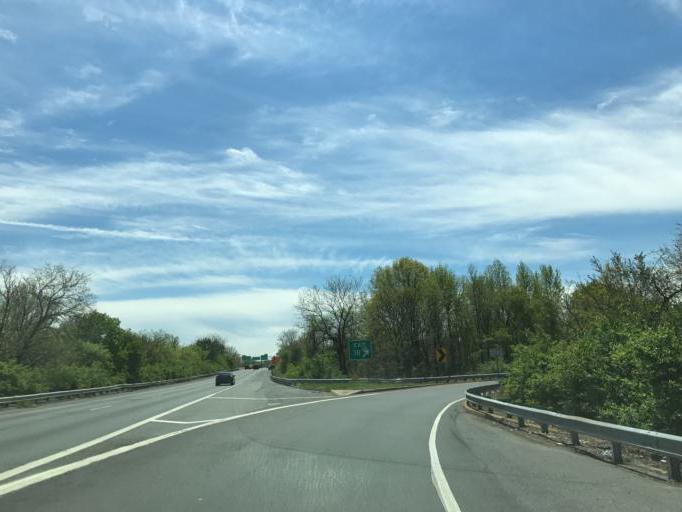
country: US
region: Delaware
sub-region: New Castle County
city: Newport
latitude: 39.7054
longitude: -75.6067
